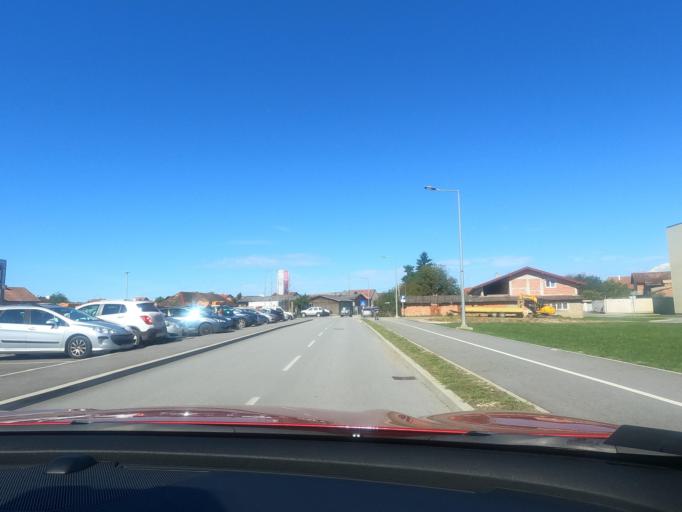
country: HR
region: Sisacko-Moslavacka
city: Petrinja
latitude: 45.4380
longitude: 16.2680
